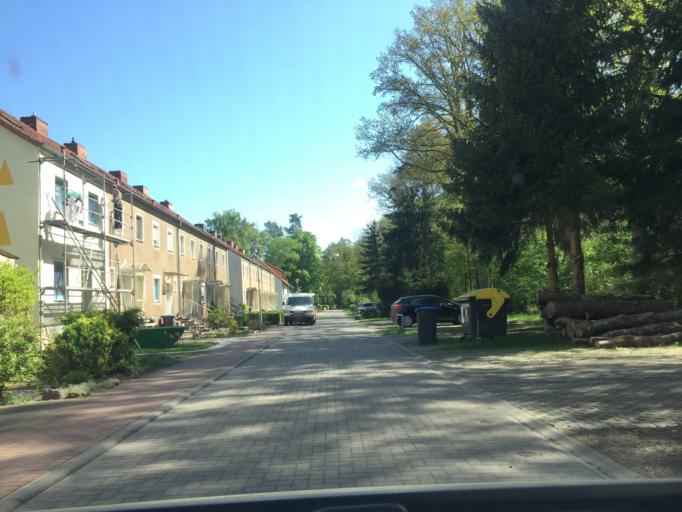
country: DE
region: Mecklenburg-Vorpommern
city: Torgelow
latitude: 53.6242
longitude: 14.0202
